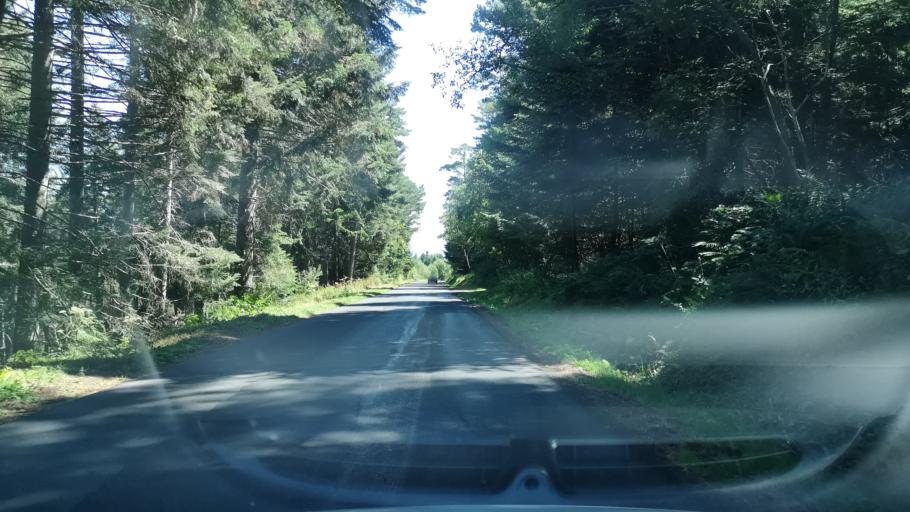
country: FR
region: Auvergne
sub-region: Departement du Puy-de-Dome
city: Mont-Dore
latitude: 45.5866
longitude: 2.8879
